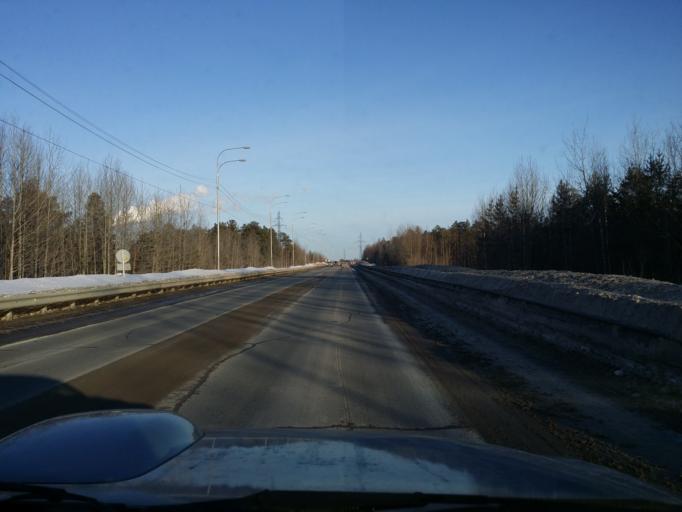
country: RU
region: Khanty-Mansiyskiy Avtonomnyy Okrug
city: Izluchinsk
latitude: 60.9646
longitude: 76.8617
